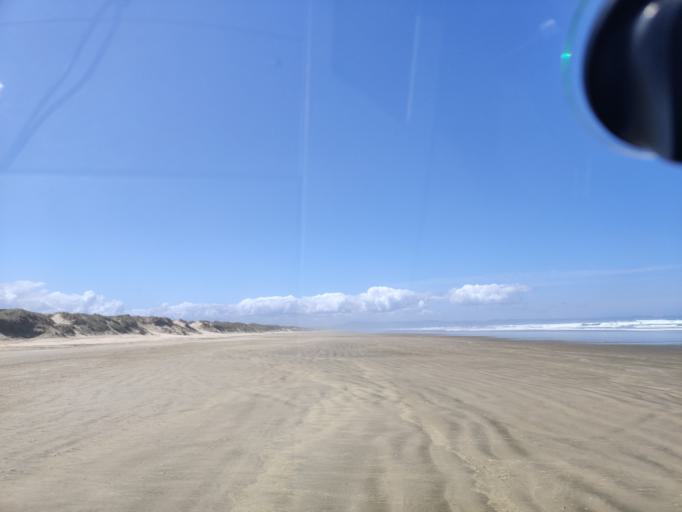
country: NZ
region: Northland
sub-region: Far North District
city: Kaitaia
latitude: -34.9543
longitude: 173.1246
